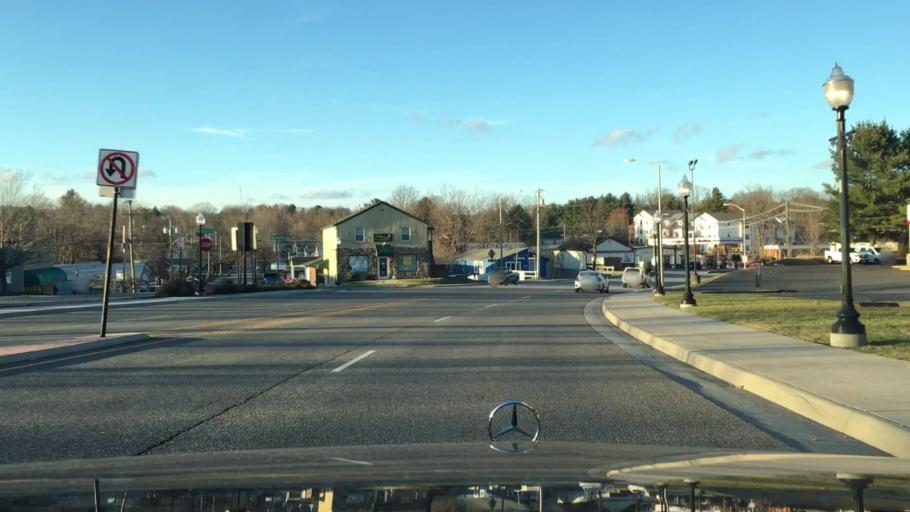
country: US
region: Virginia
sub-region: Montgomery County
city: Blacksburg
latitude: 37.2357
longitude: -80.4209
